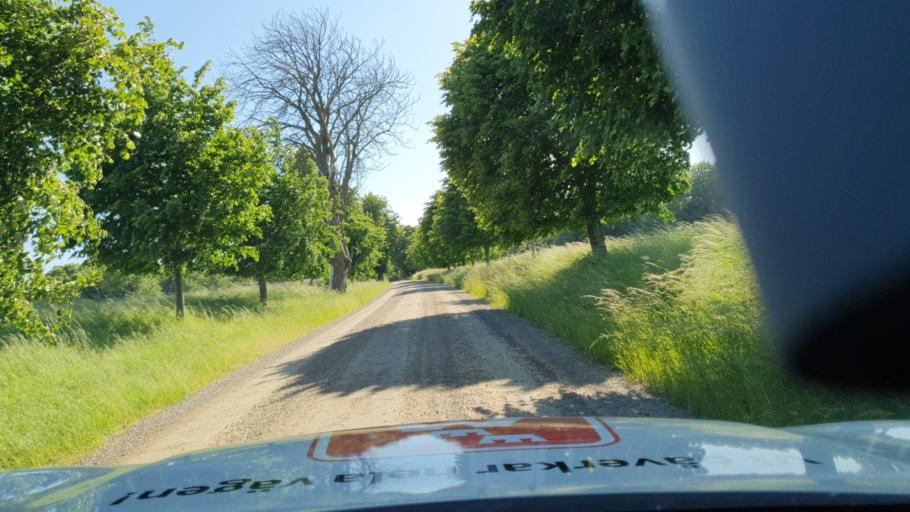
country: SE
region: Skane
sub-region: Ystads Kommun
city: Kopingebro
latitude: 55.5098
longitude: 13.8844
